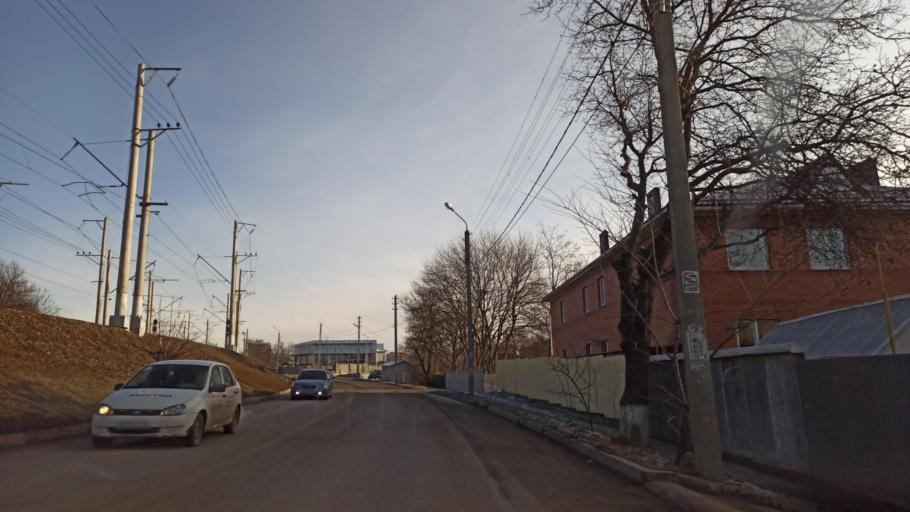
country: RU
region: Stavropol'skiy
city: Yessentuki
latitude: 44.0428
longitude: 42.8476
